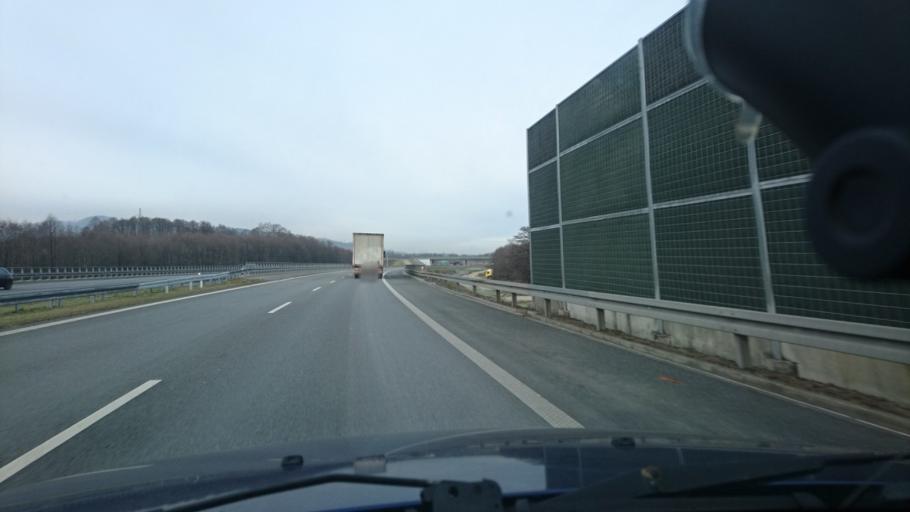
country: PL
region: Silesian Voivodeship
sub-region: Powiat bielski
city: Wilkowice
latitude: 49.7455
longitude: 19.0906
